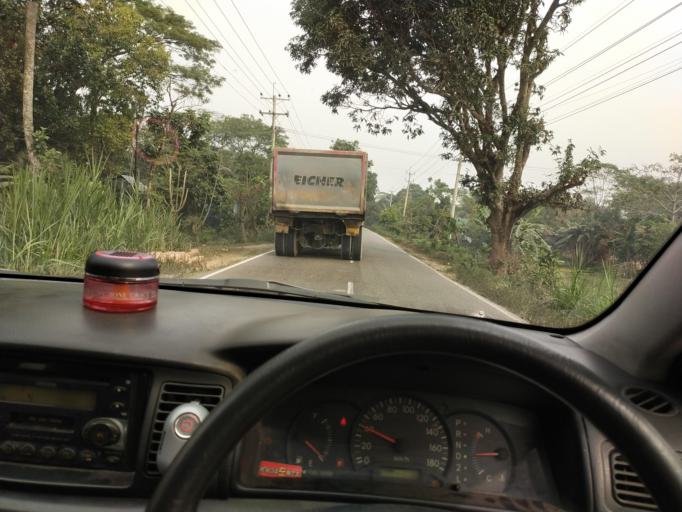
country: BD
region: Dhaka
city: Narsingdi
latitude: 24.0208
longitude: 90.7378
